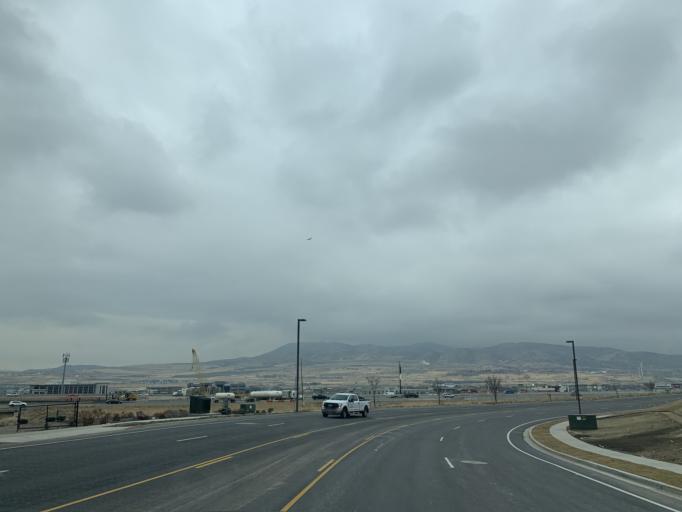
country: US
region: Utah
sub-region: Utah County
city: Lehi
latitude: 40.4327
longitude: -111.8892
